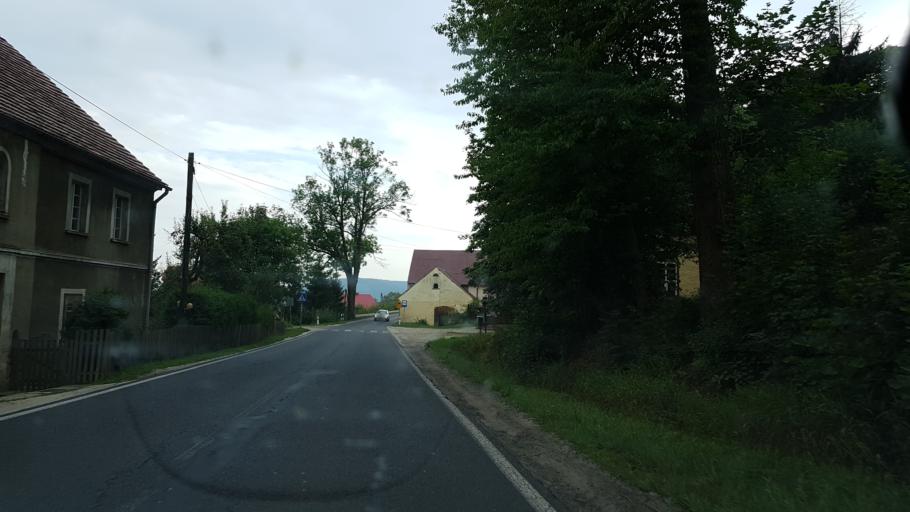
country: PL
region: Lower Silesian Voivodeship
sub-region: Powiat kamiennogorski
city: Marciszow
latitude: 50.8862
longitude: 15.9959
